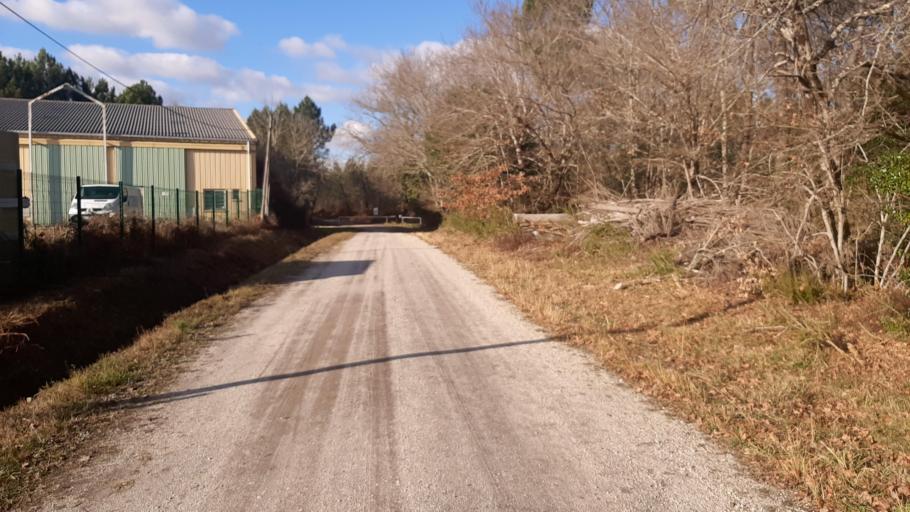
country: FR
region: Aquitaine
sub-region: Departement de la Gironde
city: Martignas-sur-Jalle
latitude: 44.8988
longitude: -0.7794
